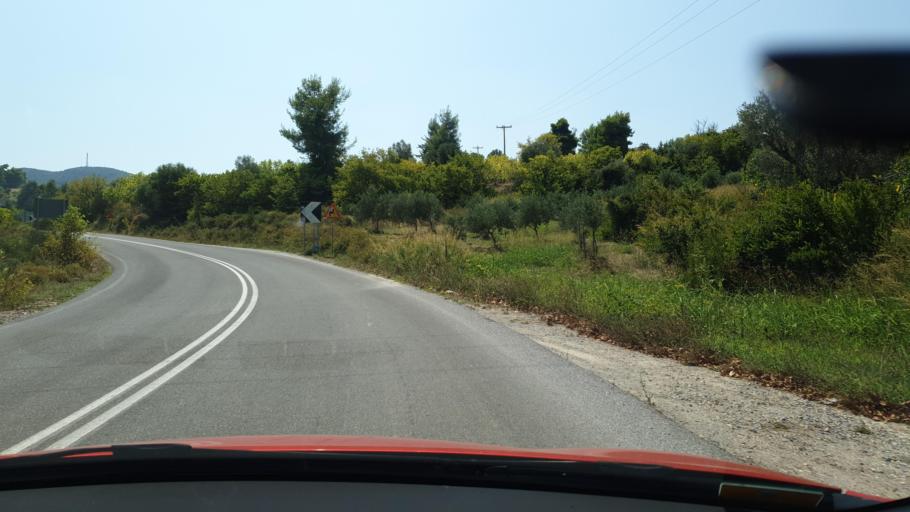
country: GR
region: Central Greece
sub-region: Nomos Evvoias
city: Oxilithos
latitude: 38.6013
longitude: 24.0754
